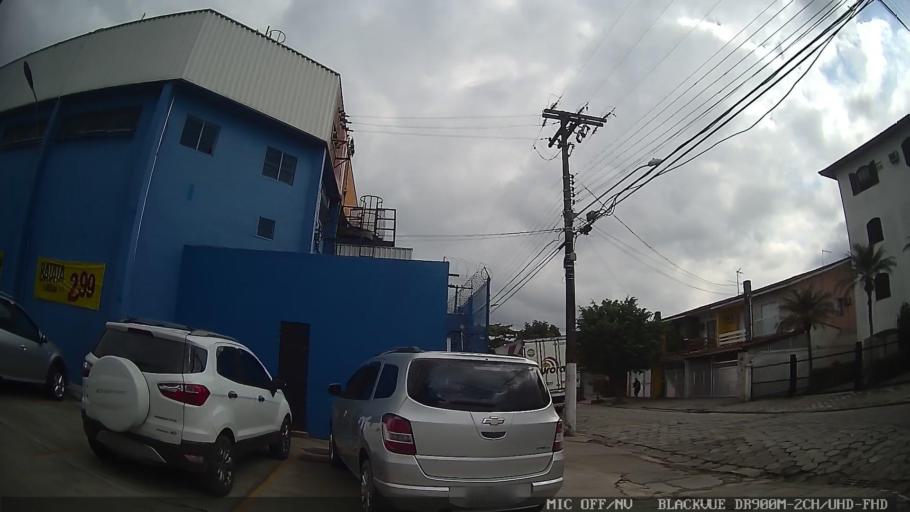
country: BR
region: Sao Paulo
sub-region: Guaruja
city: Guaruja
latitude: -23.9909
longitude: -46.2779
